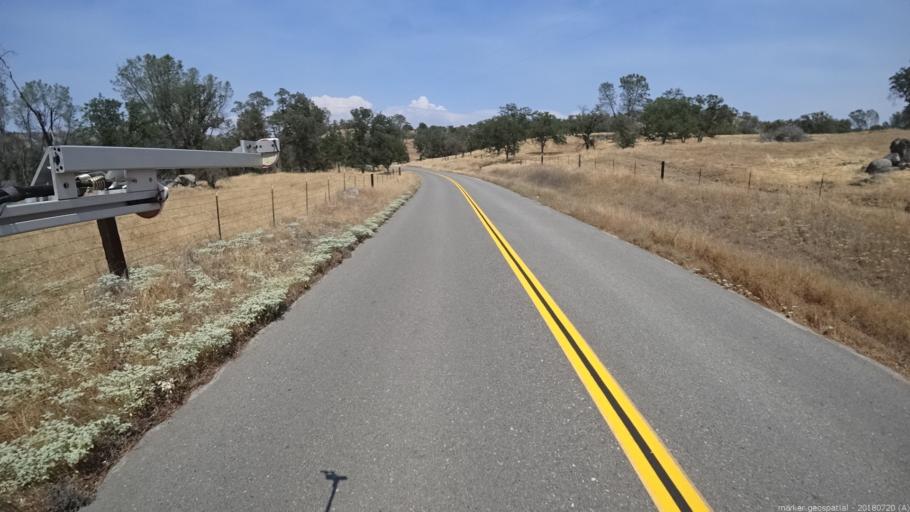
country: US
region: California
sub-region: Madera County
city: Yosemite Lakes
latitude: 37.1734
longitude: -119.8335
